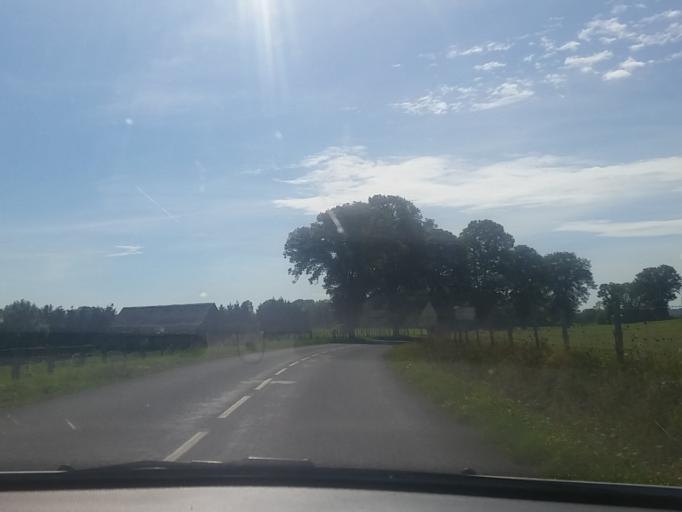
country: FR
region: Auvergne
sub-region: Departement du Cantal
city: Pierrefort
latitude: 44.9011
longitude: 2.8264
